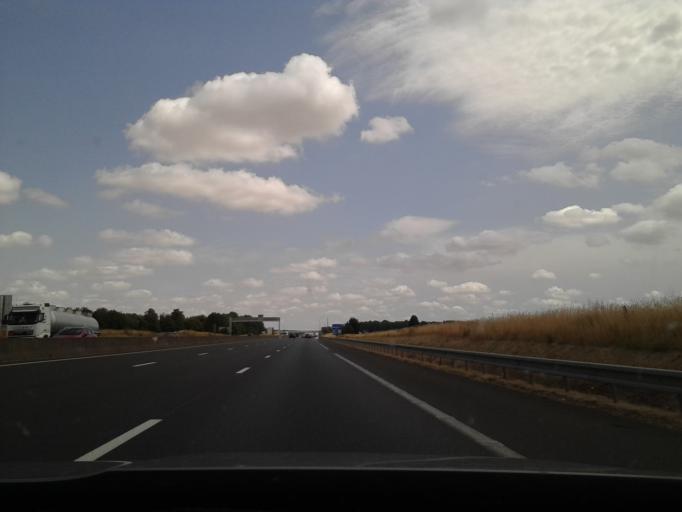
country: FR
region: Centre
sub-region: Departement d'Indre-et-Loire
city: Monnaie
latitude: 47.4866
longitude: 0.8061
